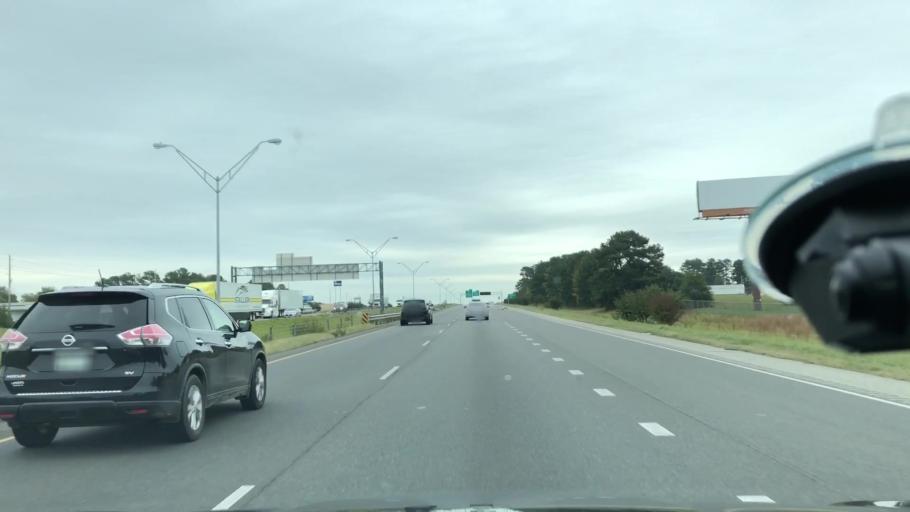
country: US
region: Arkansas
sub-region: Miller County
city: Texarkana
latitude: 33.4718
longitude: -94.0261
